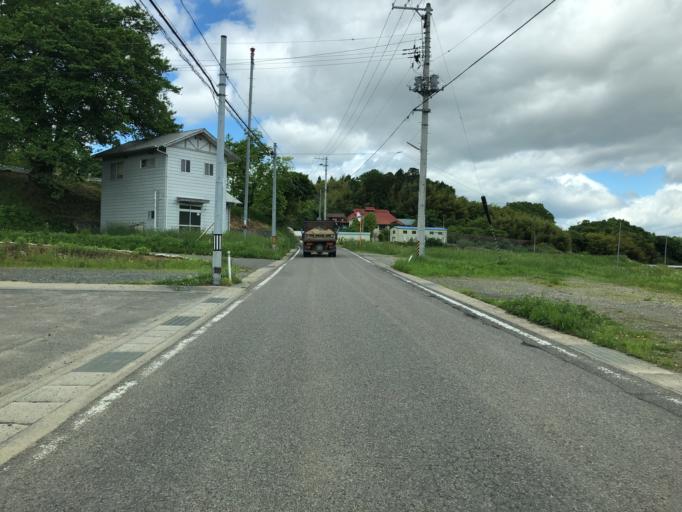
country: JP
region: Fukushima
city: Miharu
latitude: 37.4741
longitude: 140.4583
